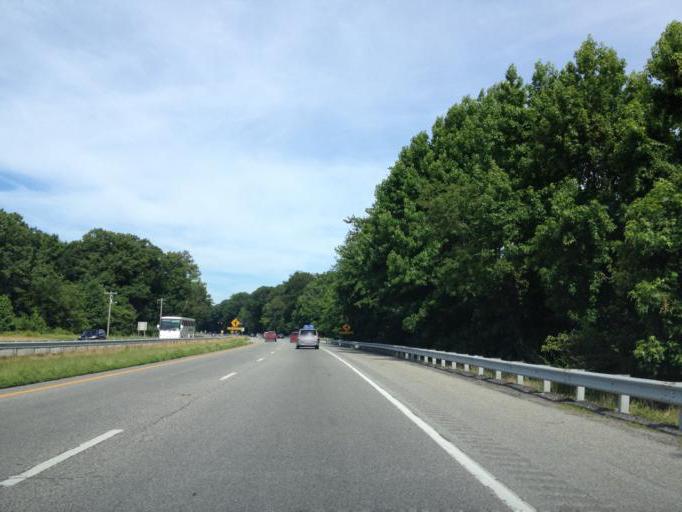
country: US
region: Maryland
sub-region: Queen Anne's County
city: Grasonville
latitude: 38.9815
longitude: -76.1444
